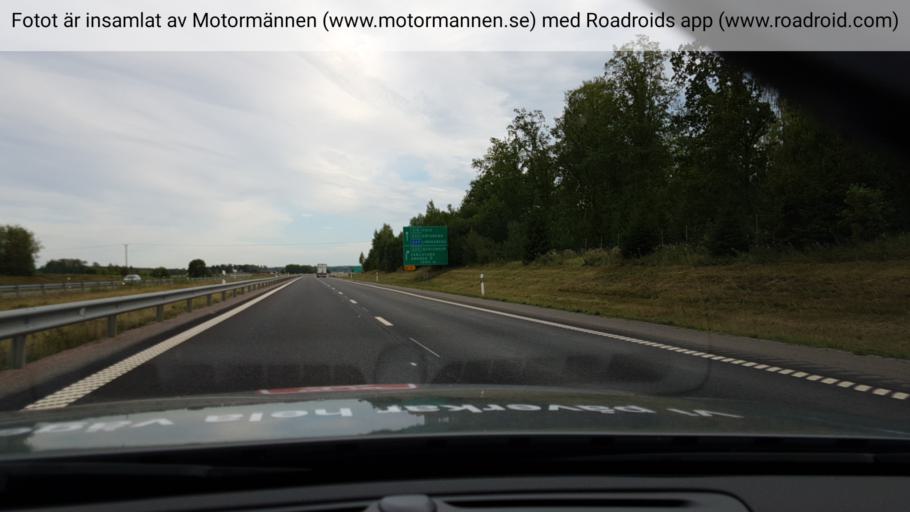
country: SE
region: Vaestmanland
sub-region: Arboga Kommun
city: Arboga
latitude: 59.4477
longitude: 15.8990
